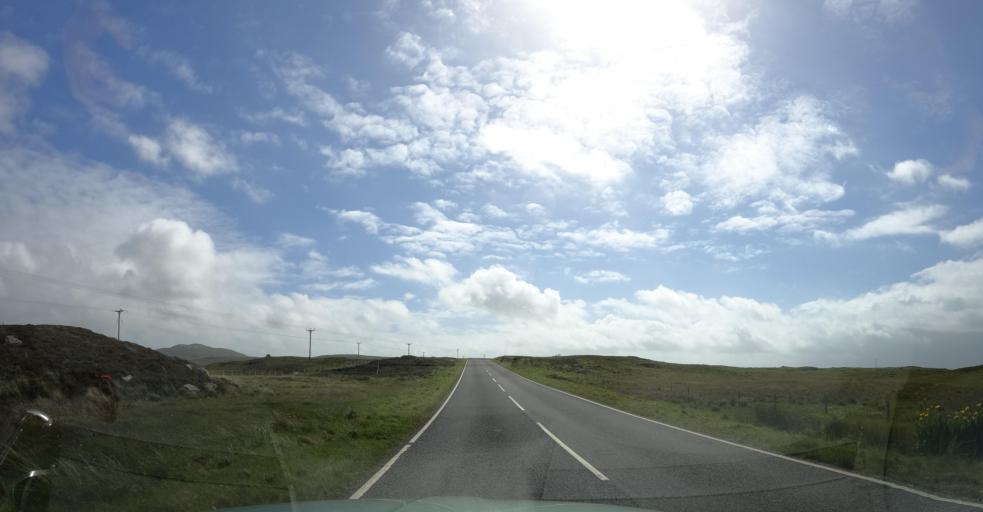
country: GB
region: Scotland
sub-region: Eilean Siar
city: Isle of South Uist
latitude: 57.2465
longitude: -7.3818
